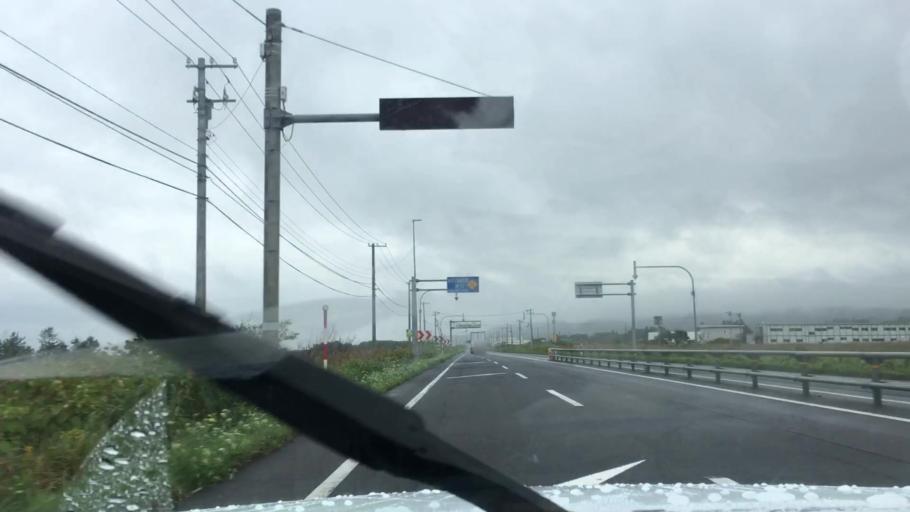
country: JP
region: Hokkaido
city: Niseko Town
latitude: 42.3980
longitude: 140.3019
